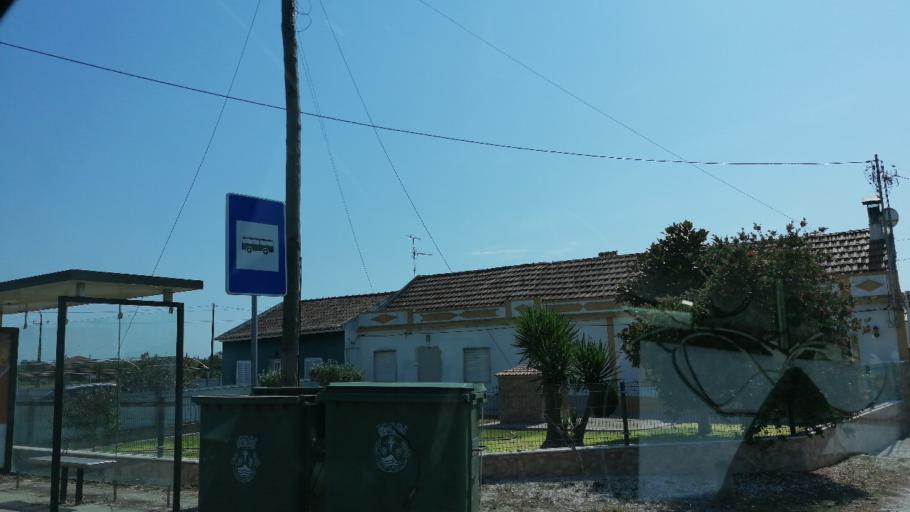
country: PT
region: Santarem
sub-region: Benavente
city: Poceirao
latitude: 38.7406
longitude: -8.6579
